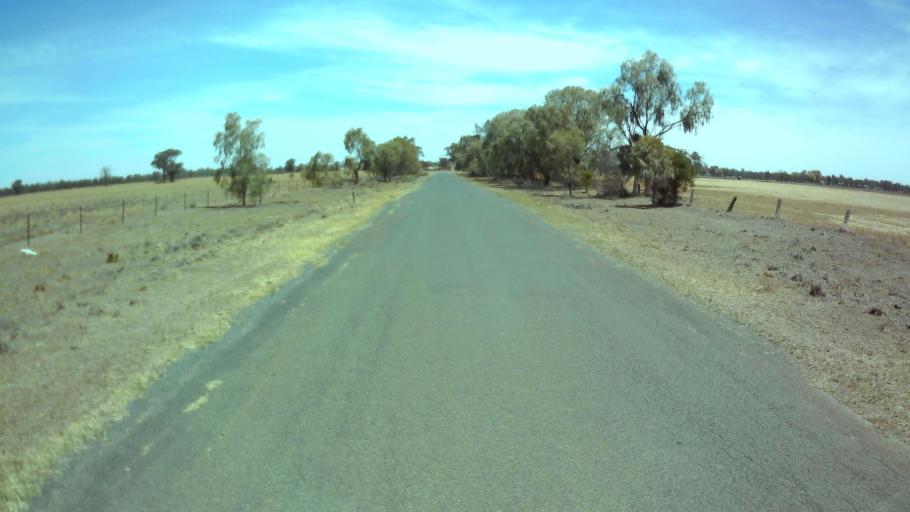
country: AU
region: New South Wales
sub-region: Weddin
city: Grenfell
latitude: -33.8280
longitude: 147.7463
